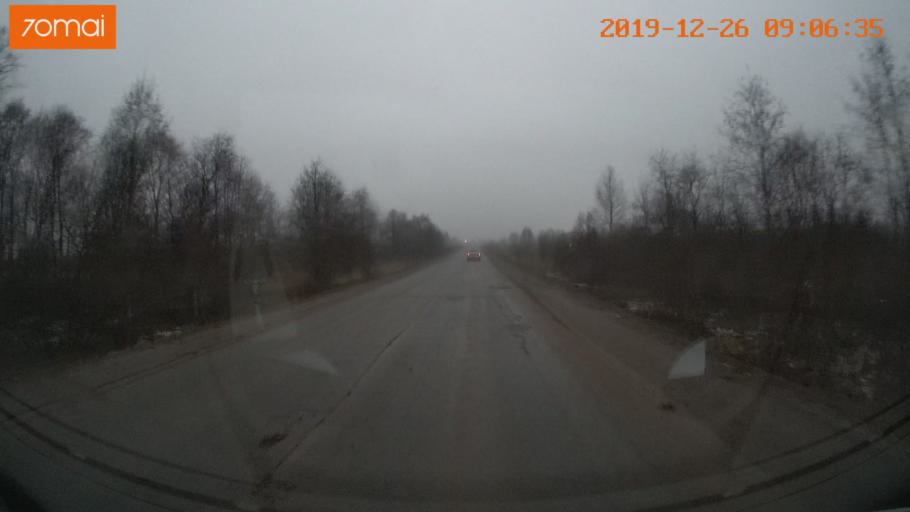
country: RU
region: Vologda
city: Gryazovets
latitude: 58.8373
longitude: 40.2527
